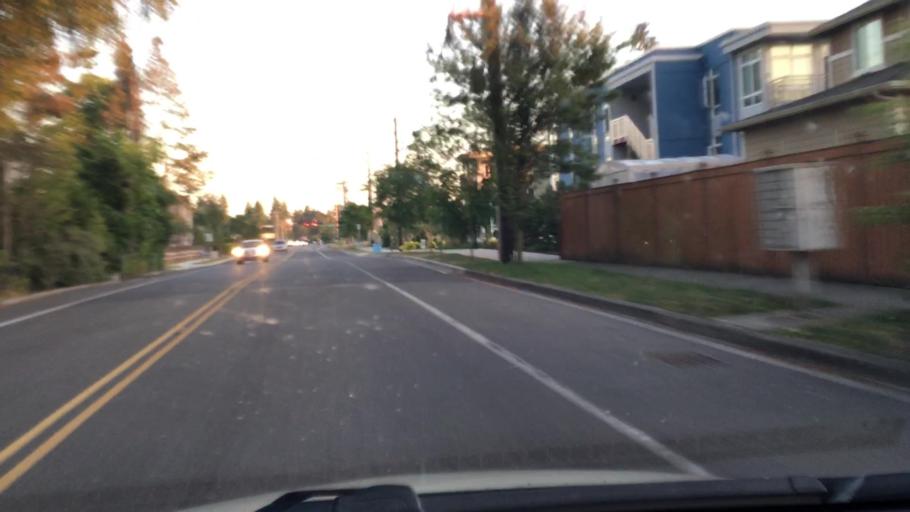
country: US
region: Washington
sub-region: Snohomish County
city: Martha Lake
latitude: 47.8521
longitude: -122.2517
